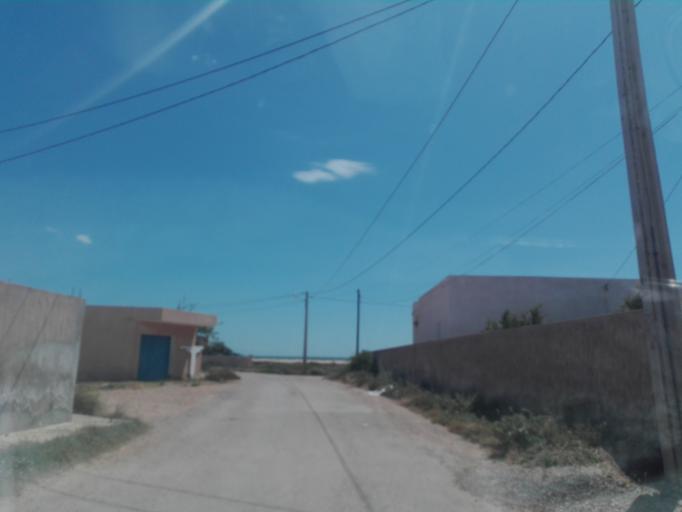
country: TN
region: Safaqis
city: Jabinyanah
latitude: 34.8166
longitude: 11.2624
